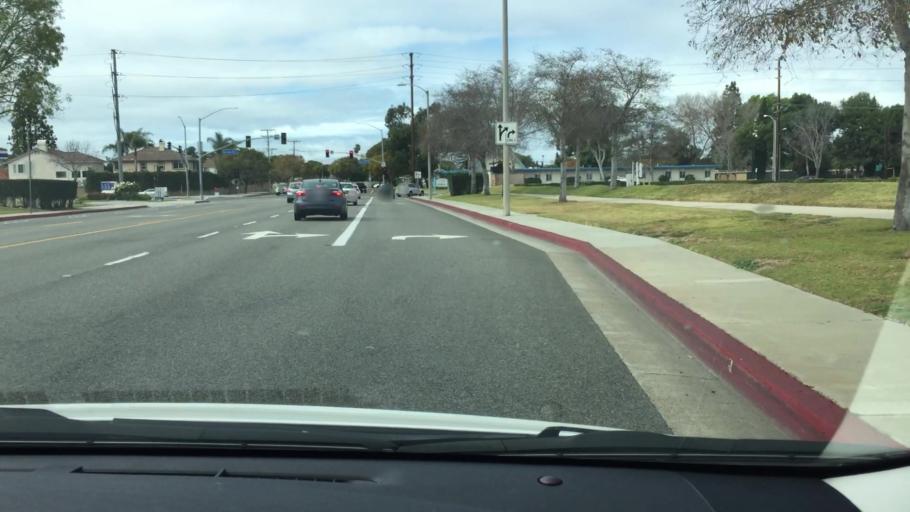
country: US
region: California
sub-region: Orange County
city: Costa Mesa
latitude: 33.6639
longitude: -117.9063
